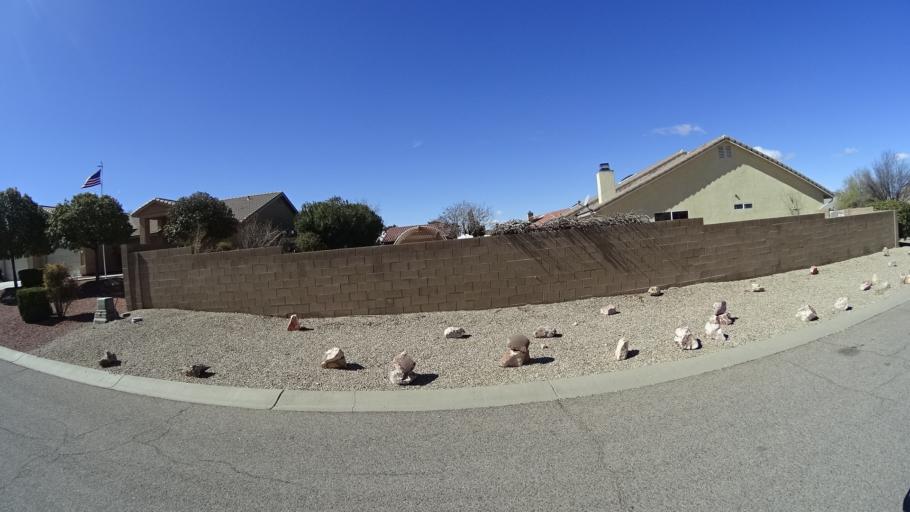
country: US
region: Arizona
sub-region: Mohave County
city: Kingman
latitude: 35.2027
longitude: -113.9595
